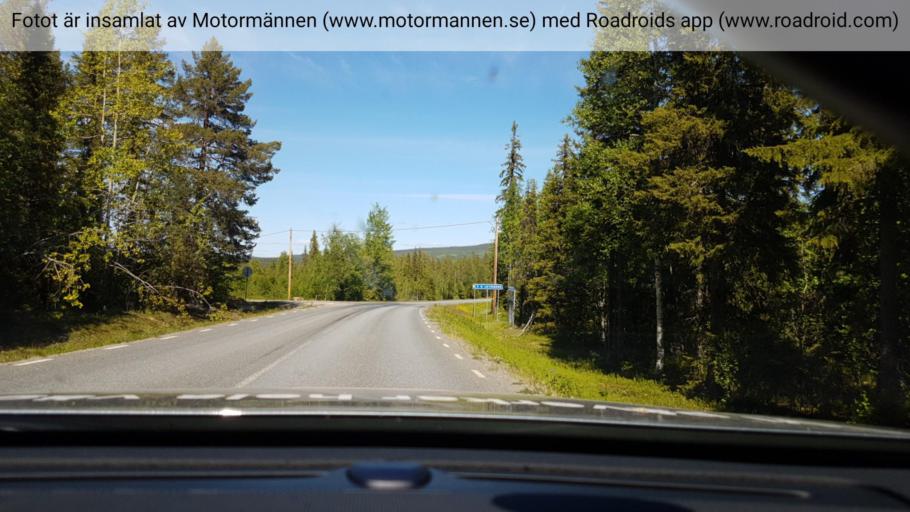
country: SE
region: Vaesterbotten
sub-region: Vilhelmina Kommun
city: Vilhelmina
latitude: 64.6524
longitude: 17.0838
